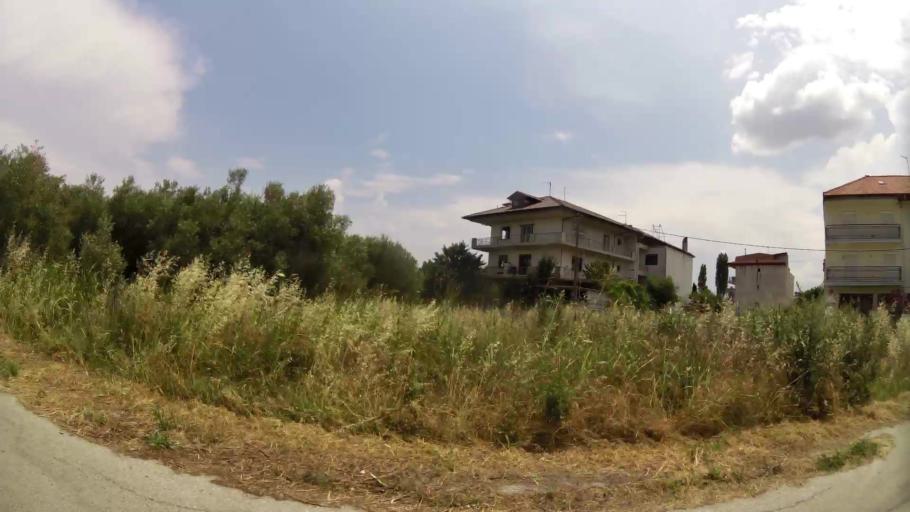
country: GR
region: Central Macedonia
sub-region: Nomos Pierias
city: Peristasi
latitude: 40.2752
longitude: 22.5464
